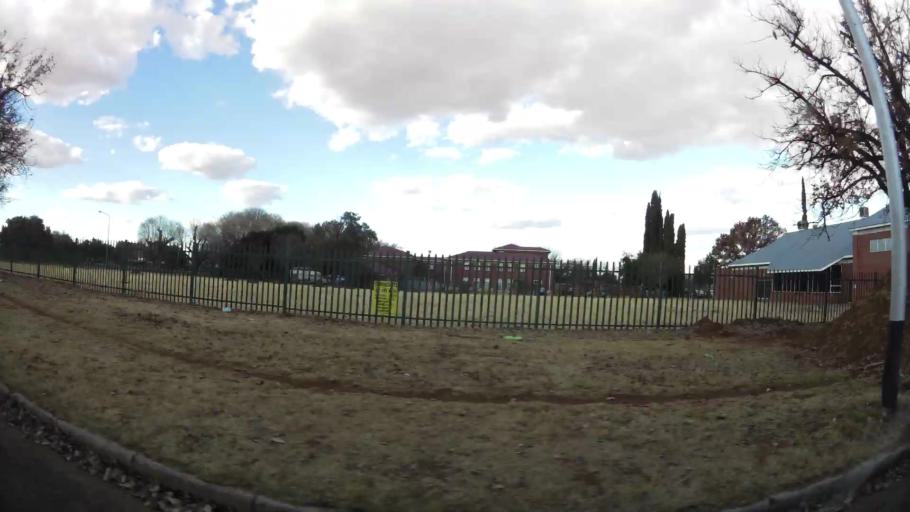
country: ZA
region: North-West
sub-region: Dr Kenneth Kaunda District Municipality
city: Potchefstroom
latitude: -26.7174
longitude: 27.0888
